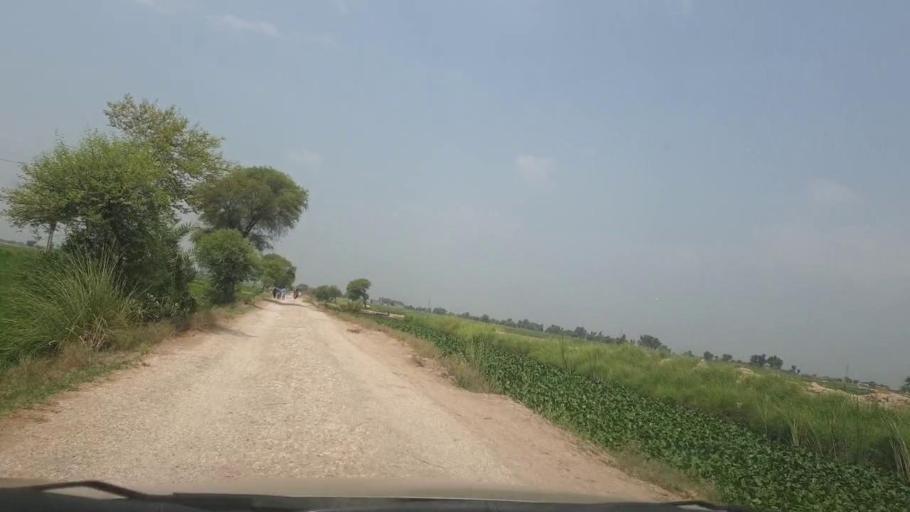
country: PK
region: Sindh
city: Naudero
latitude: 27.6874
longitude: 68.2587
